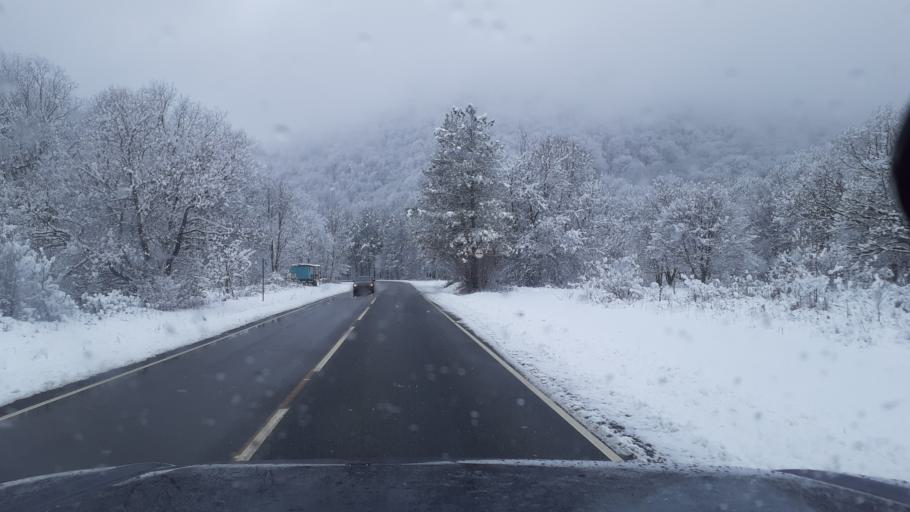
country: RU
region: Adygeya
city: Kamennomostskiy
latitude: 44.1736
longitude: 40.1506
